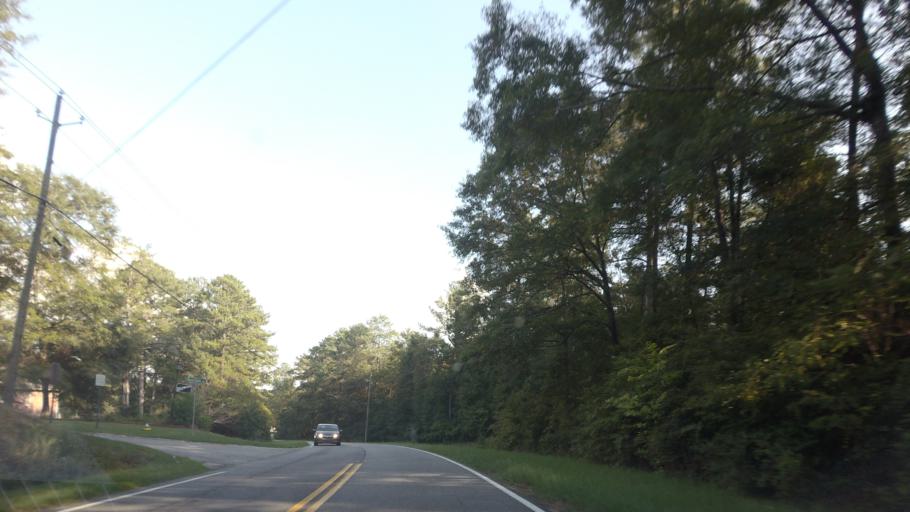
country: US
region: Georgia
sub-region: Bibb County
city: Macon
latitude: 32.8609
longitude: -83.7234
